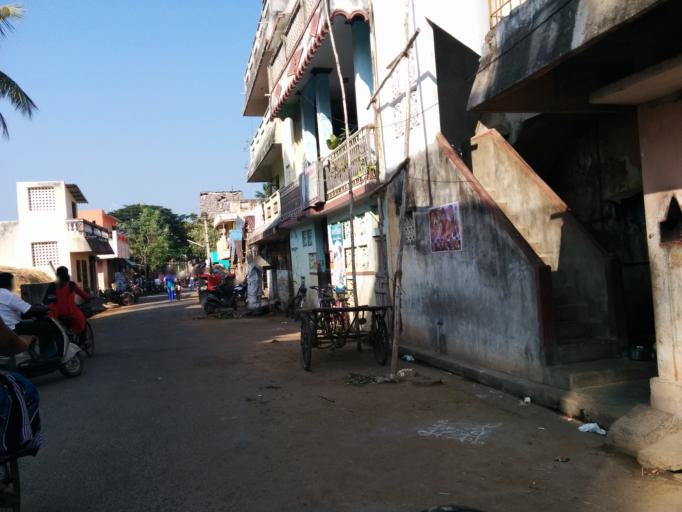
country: IN
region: Pondicherry
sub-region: Puducherry
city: Puducherry
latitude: 11.9473
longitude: 79.8347
